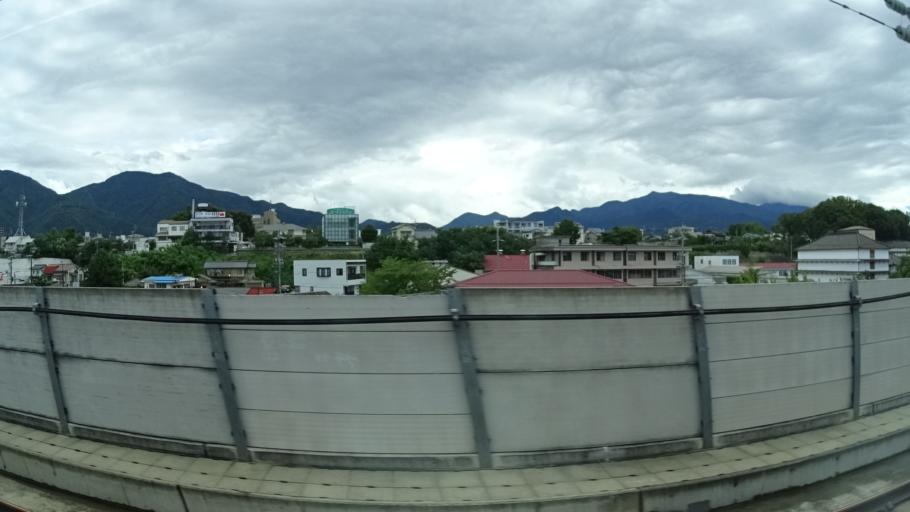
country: JP
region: Nagano
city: Ueda
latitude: 36.3999
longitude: 138.2456
